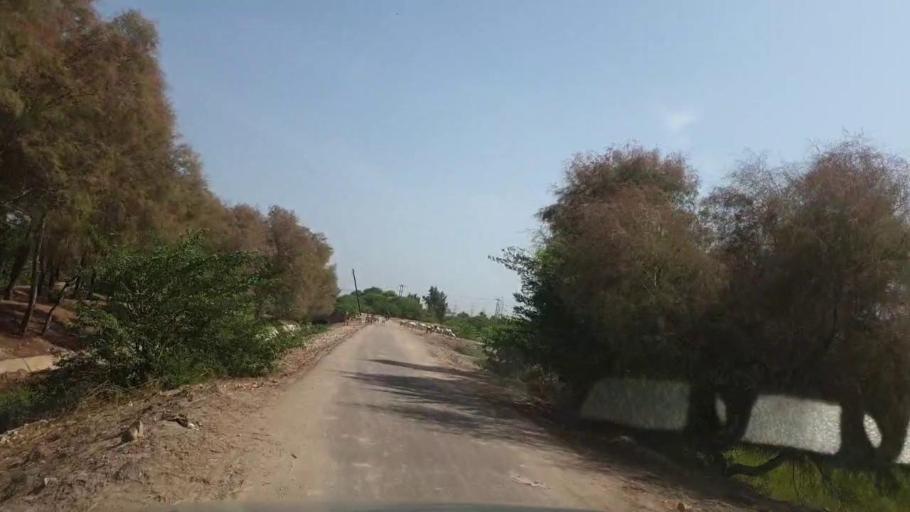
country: PK
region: Sindh
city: Rohri
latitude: 27.6723
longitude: 68.8823
